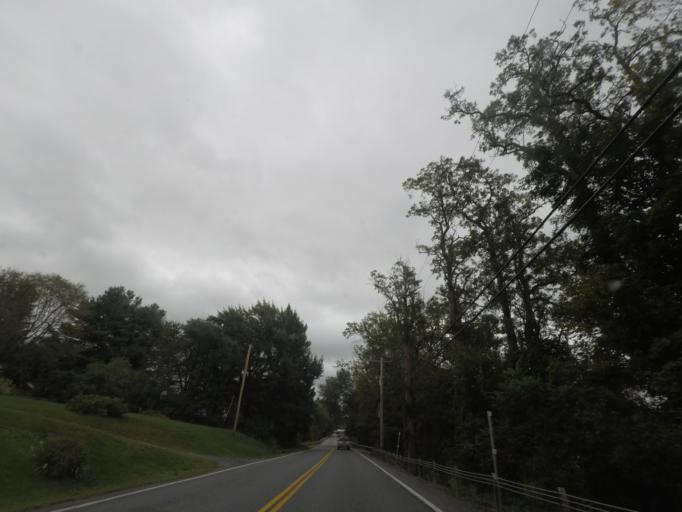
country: US
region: New York
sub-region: Rensselaer County
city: Hoosick Falls
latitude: 42.9514
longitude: -73.3846
